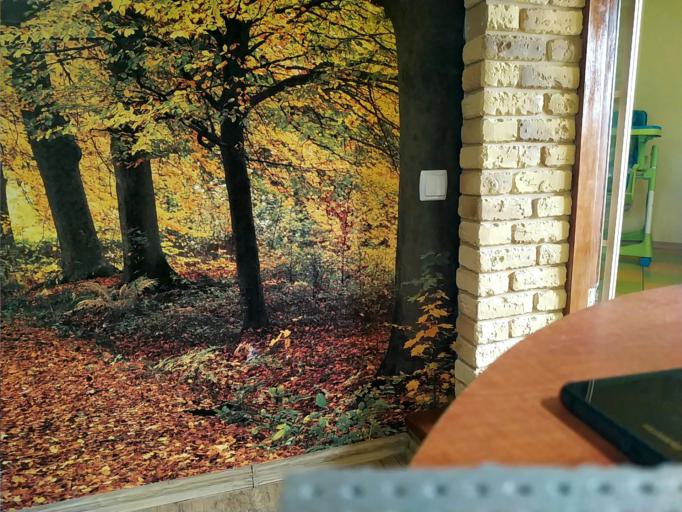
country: RU
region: Tverskaya
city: Kalashnikovo
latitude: 57.3164
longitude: 35.1109
